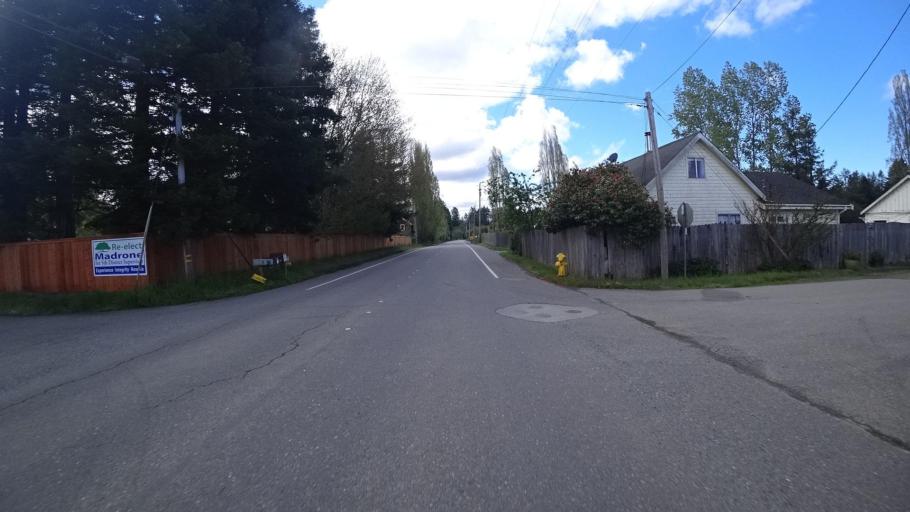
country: US
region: California
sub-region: Humboldt County
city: McKinleyville
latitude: 40.9657
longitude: -124.0360
